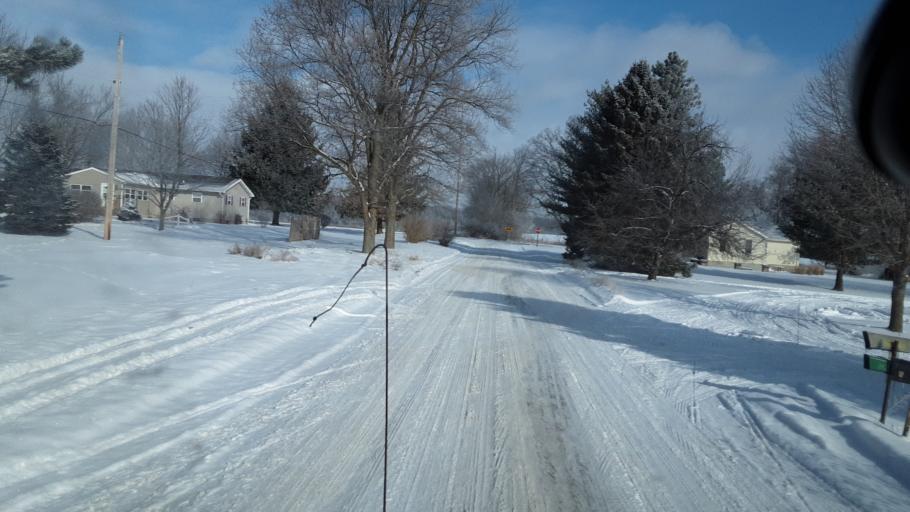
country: US
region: Michigan
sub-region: Eaton County
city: Eaton Rapids
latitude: 42.5228
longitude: -84.6310
